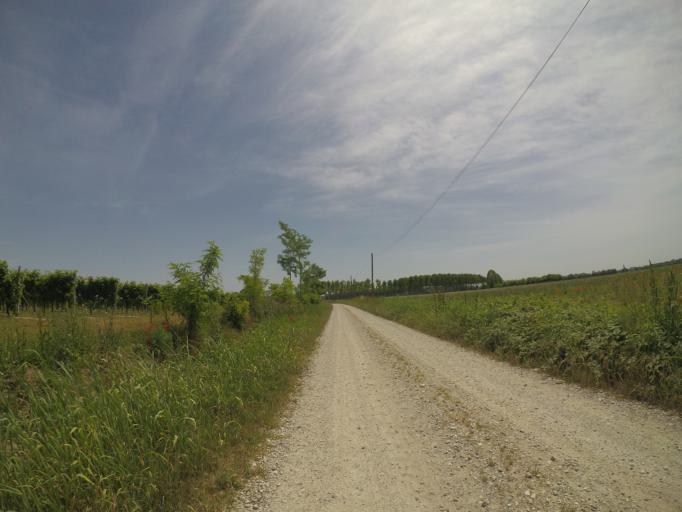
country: IT
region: Friuli Venezia Giulia
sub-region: Provincia di Udine
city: Camino al Tagliamento
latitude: 45.9107
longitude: 12.9561
